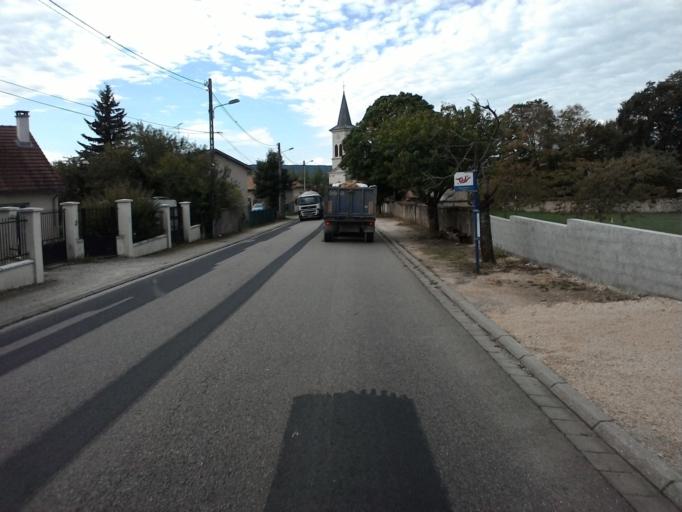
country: FR
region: Lorraine
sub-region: Departement de Meurthe-et-Moselle
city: Ecrouves
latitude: 48.7673
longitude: 5.8648
